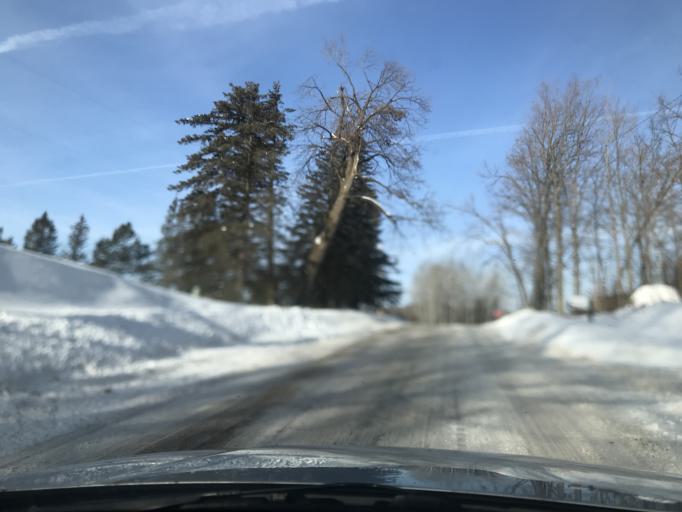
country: US
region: Wisconsin
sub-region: Menominee County
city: Legend Lake
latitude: 45.3002
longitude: -88.4917
